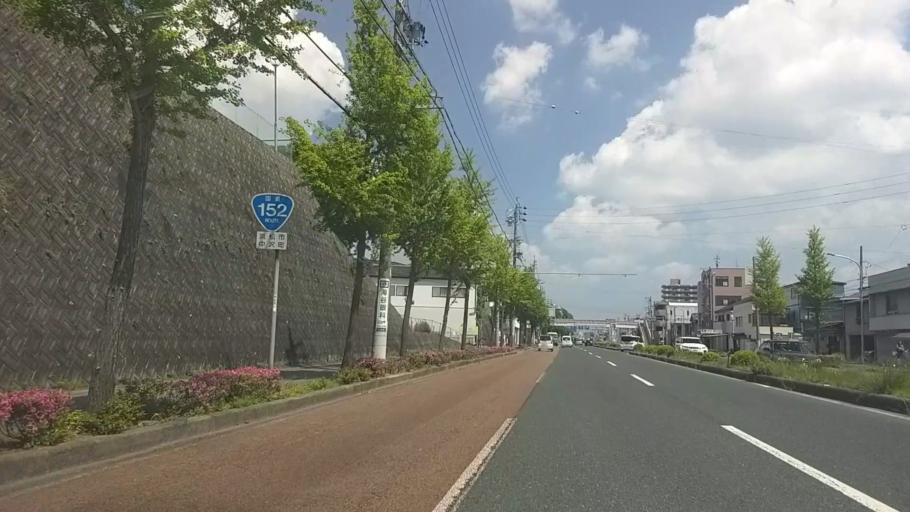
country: JP
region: Shizuoka
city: Hamamatsu
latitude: 34.7191
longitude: 137.7290
